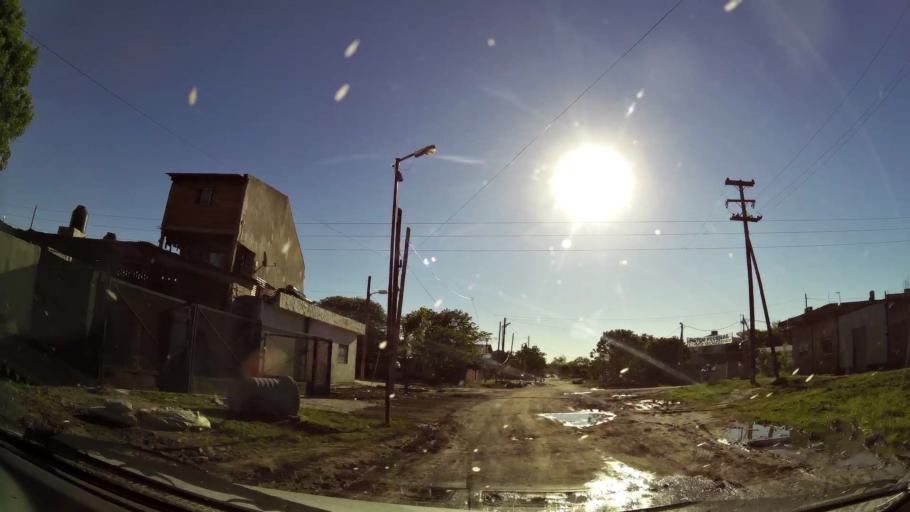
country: AR
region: Buenos Aires
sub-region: Partido de Quilmes
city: Quilmes
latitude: -34.7467
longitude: -58.3195
